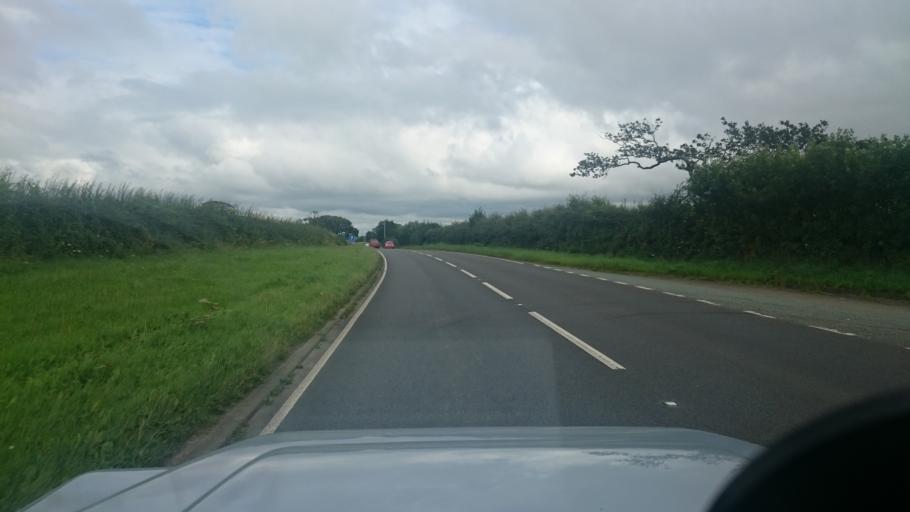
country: GB
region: Wales
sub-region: Pembrokeshire
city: Wiston
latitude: 51.8001
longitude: -4.8465
